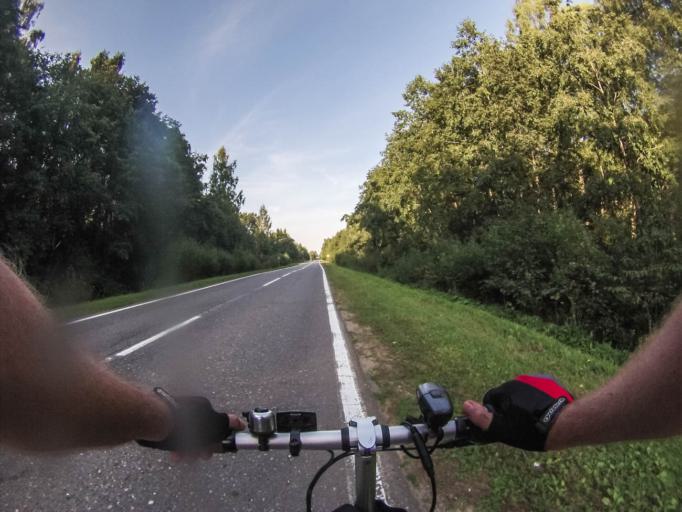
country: RU
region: Jaroslavl
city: Myshkin
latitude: 57.7192
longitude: 38.4101
